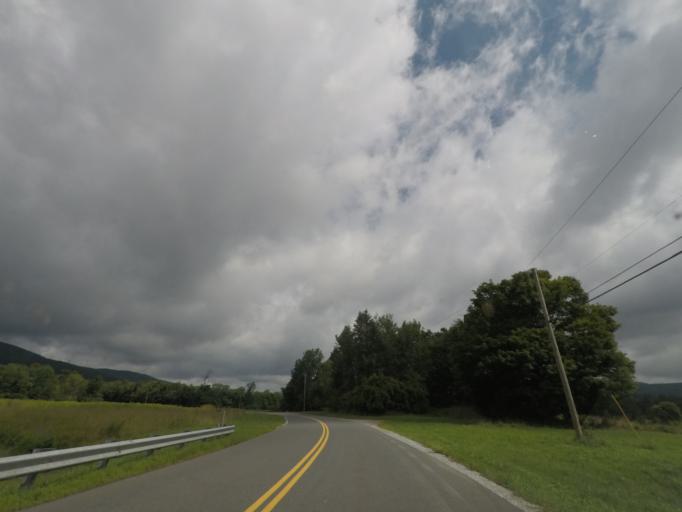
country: US
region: Massachusetts
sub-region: Berkshire County
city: Lanesborough
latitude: 42.5594
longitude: -73.2503
